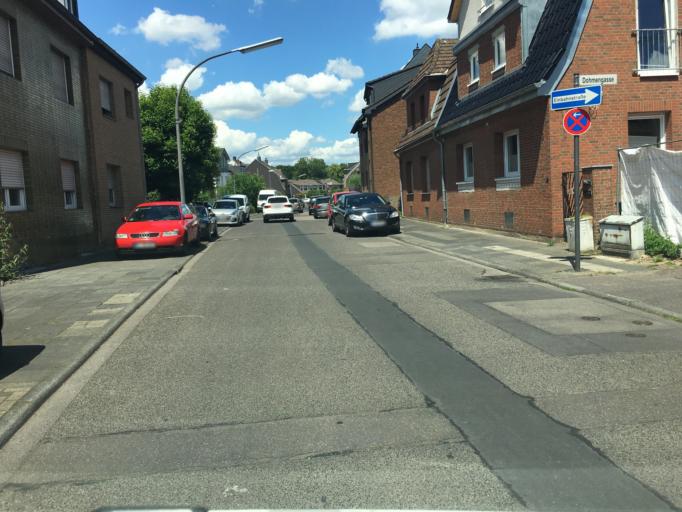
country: DE
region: North Rhine-Westphalia
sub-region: Regierungsbezirk Koln
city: Mengenich
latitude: 50.9812
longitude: 6.8577
